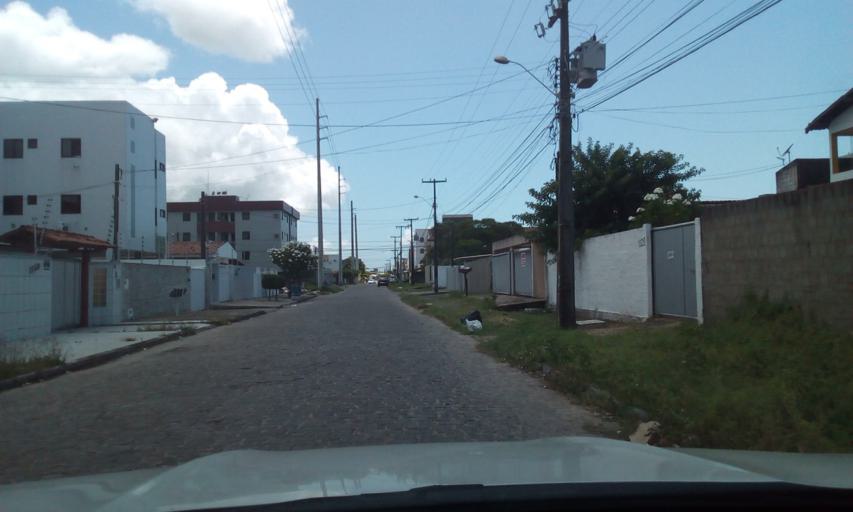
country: BR
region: Paraiba
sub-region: Joao Pessoa
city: Joao Pessoa
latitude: -7.0659
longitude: -34.8470
